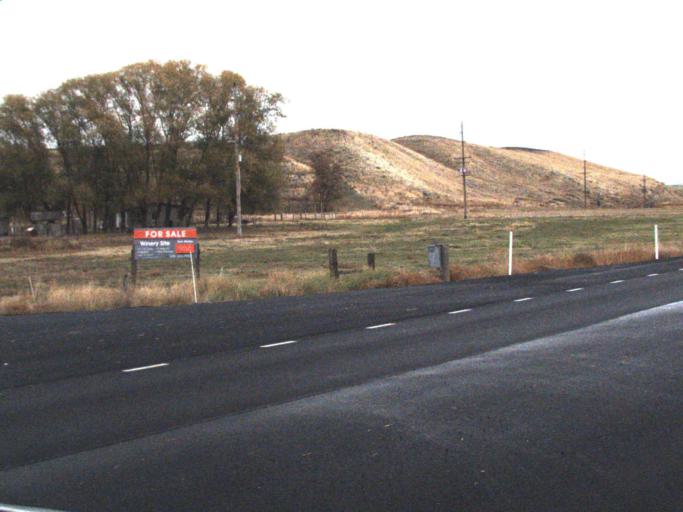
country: US
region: Washington
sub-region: Walla Walla County
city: Garrett
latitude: 46.0558
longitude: -118.5803
